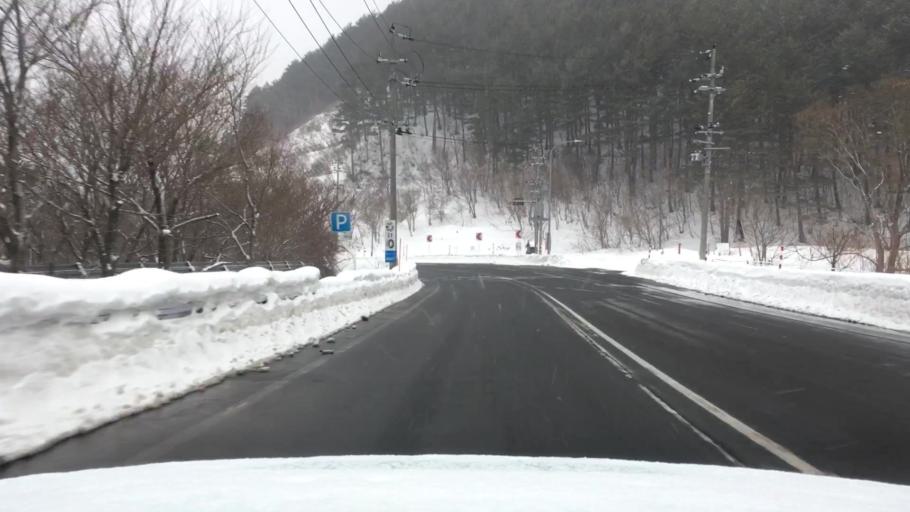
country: JP
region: Akita
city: Hanawa
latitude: 40.0236
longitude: 140.9863
